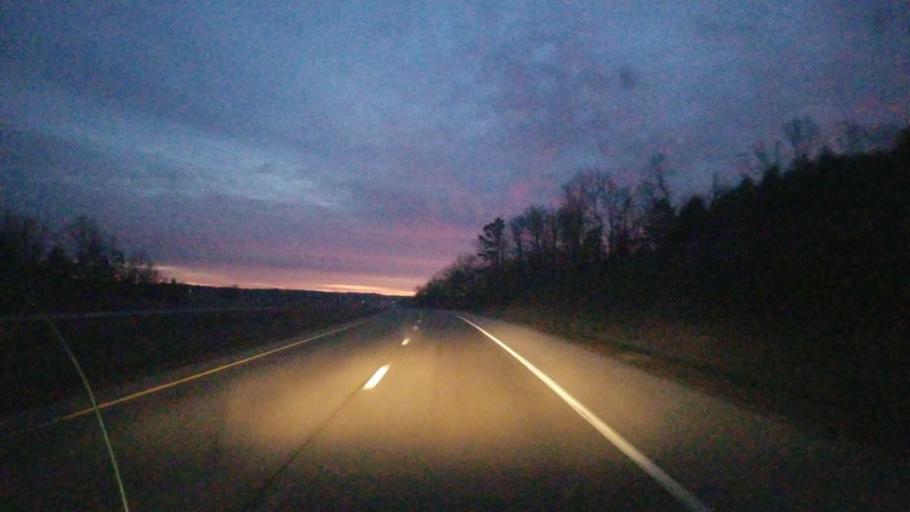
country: US
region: Missouri
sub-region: Howell County
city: Mountain View
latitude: 36.9915
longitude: -91.5210
